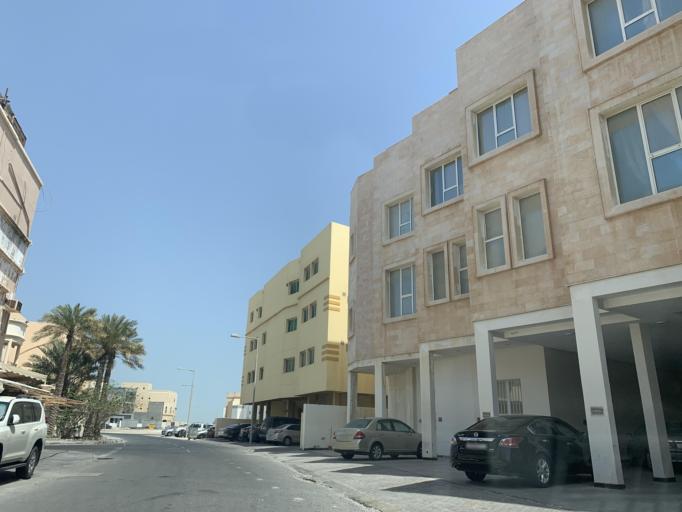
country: BH
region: Muharraq
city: Al Muharraq
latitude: 26.2783
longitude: 50.6077
